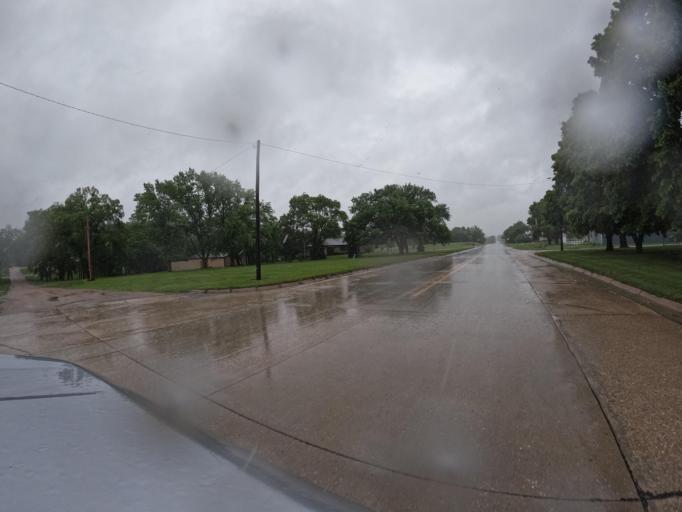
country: US
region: Nebraska
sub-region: Gage County
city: Wymore
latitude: 40.1182
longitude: -96.6715
